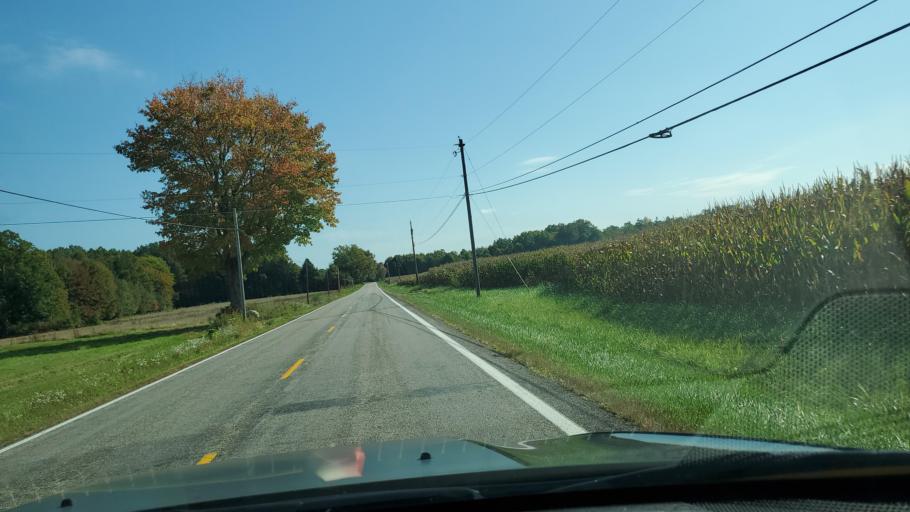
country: US
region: Ohio
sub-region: Trumbull County
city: Cortland
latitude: 41.3886
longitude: -80.6247
